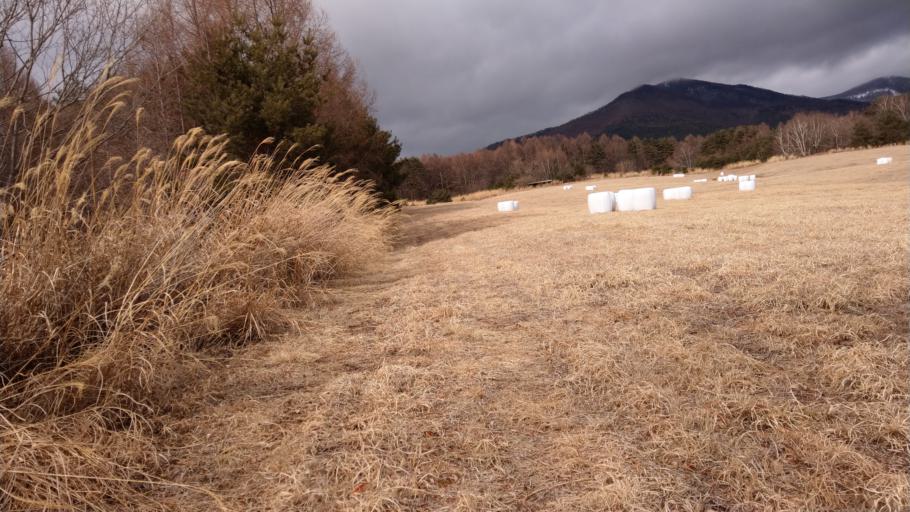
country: JP
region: Nagano
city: Komoro
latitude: 36.3660
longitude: 138.4379
